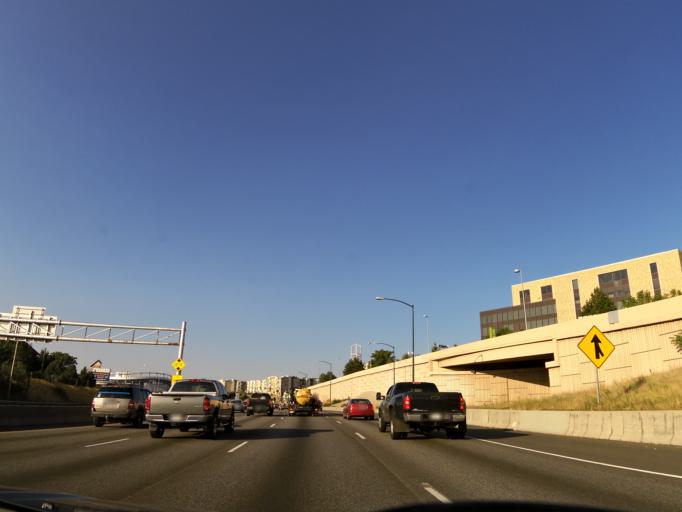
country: US
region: Colorado
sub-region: Denver County
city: Denver
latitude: 39.7540
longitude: -105.0146
